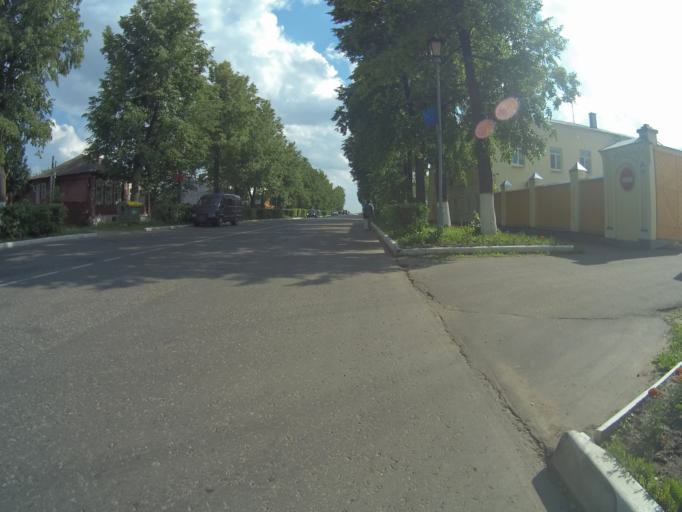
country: RU
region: Vladimir
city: Suzdal'
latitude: 56.4090
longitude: 40.4464
